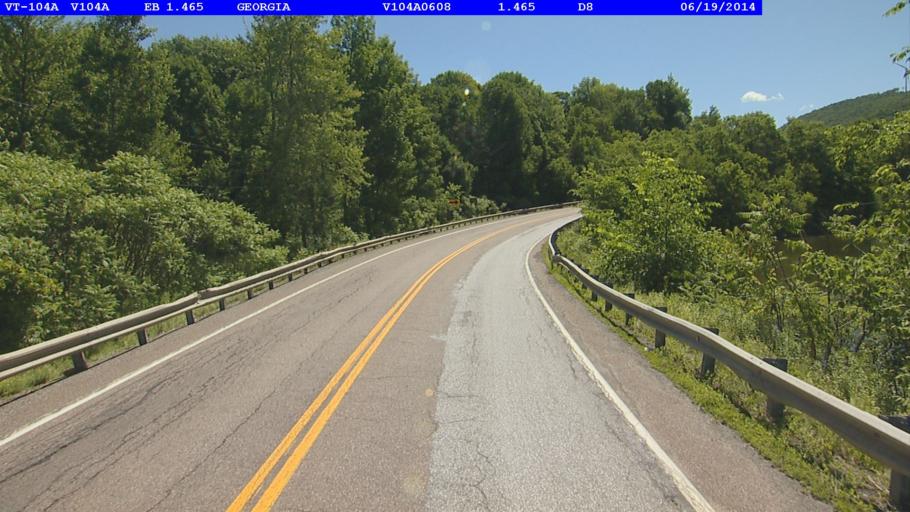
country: US
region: Vermont
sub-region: Chittenden County
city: Milton
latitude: 44.6822
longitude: -73.0862
